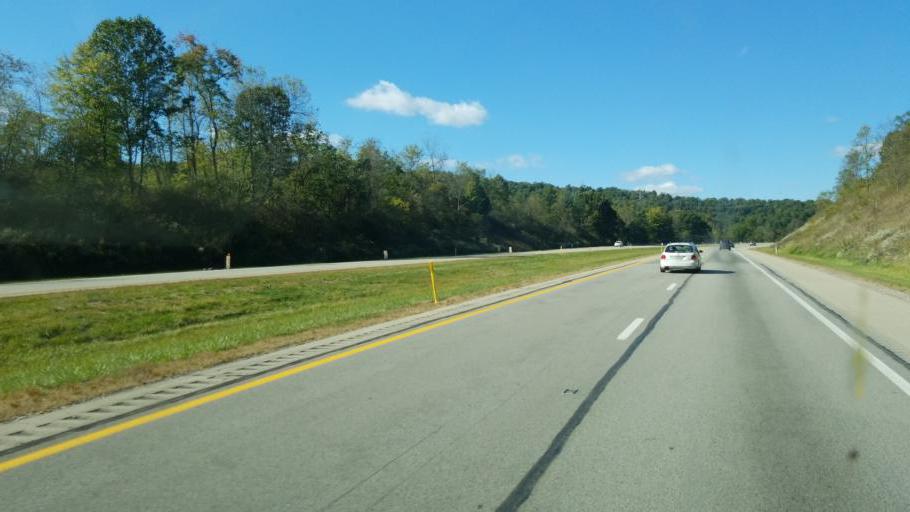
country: US
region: Pennsylvania
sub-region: Greene County
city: Morrisville
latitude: 39.7734
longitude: -80.0811
